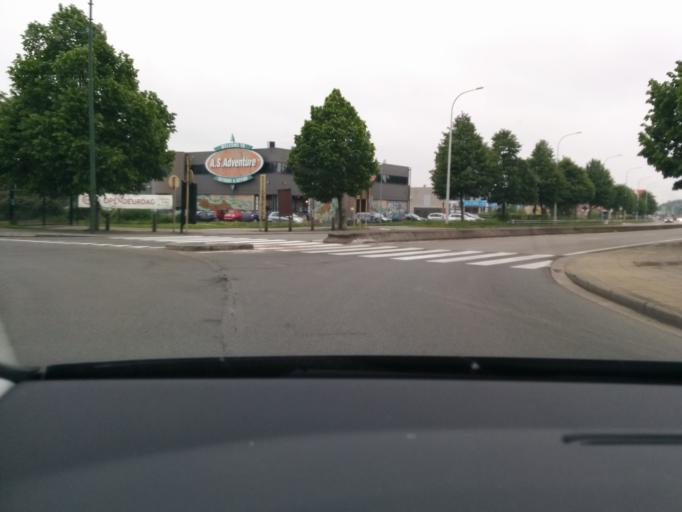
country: BE
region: Flanders
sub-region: Provincie Vlaams-Brabant
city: Drogenbos
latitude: 50.7957
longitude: 4.3175
